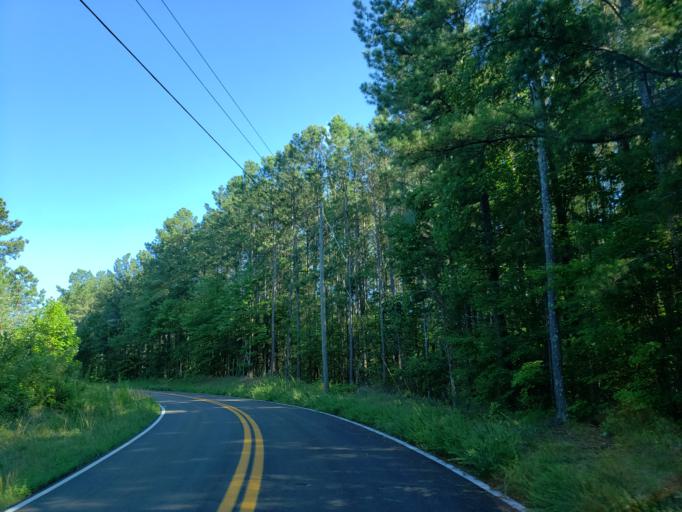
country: US
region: Georgia
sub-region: Bartow County
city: Rydal
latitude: 34.3702
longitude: -84.6271
